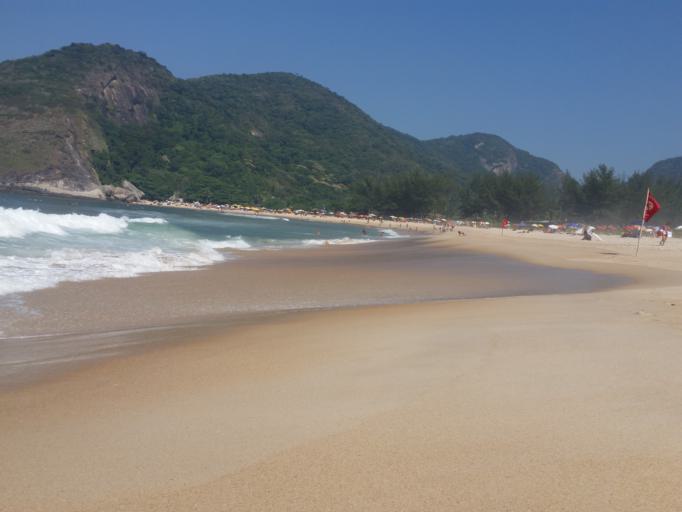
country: BR
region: Rio de Janeiro
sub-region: Nilopolis
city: Nilopolis
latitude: -23.0501
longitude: -43.5329
